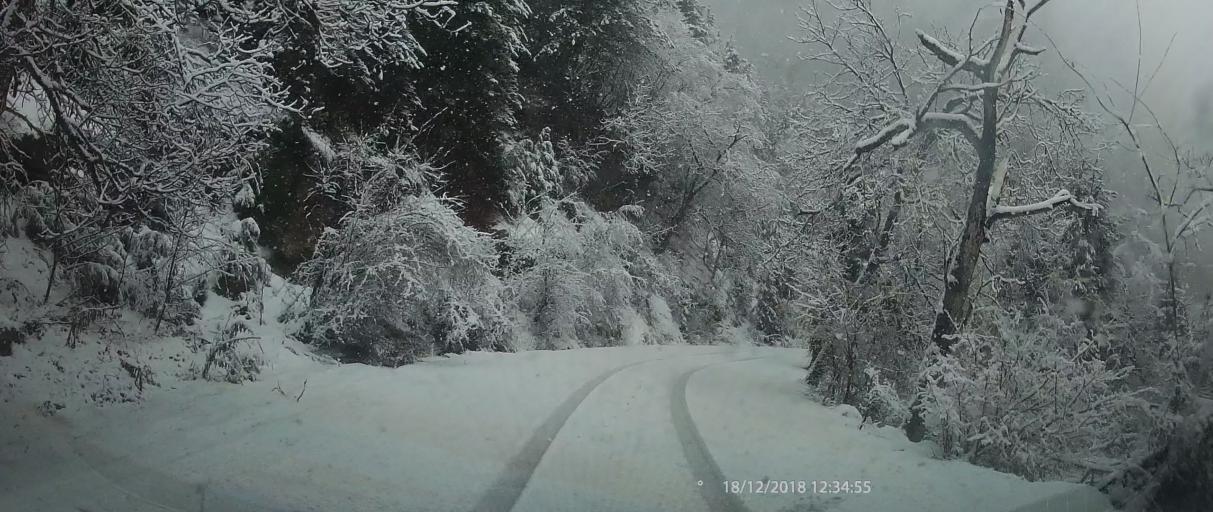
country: GR
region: Central Macedonia
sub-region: Nomos Pierias
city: Litochoro
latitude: 40.0860
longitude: 22.4069
